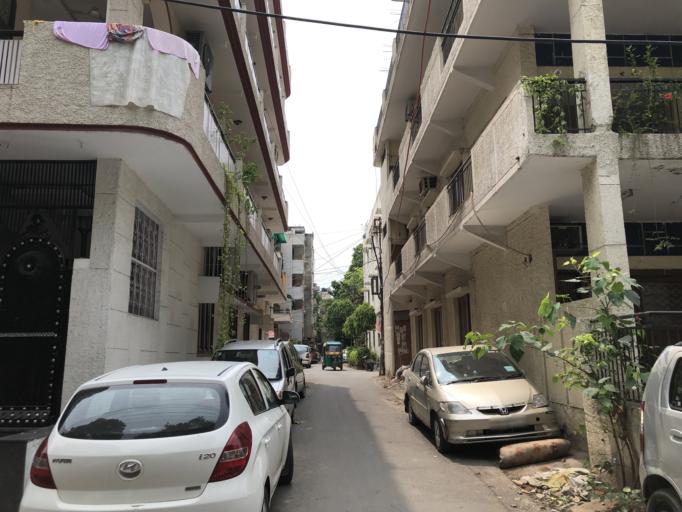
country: IN
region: NCT
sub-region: New Delhi
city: New Delhi
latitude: 28.5777
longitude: 77.2432
